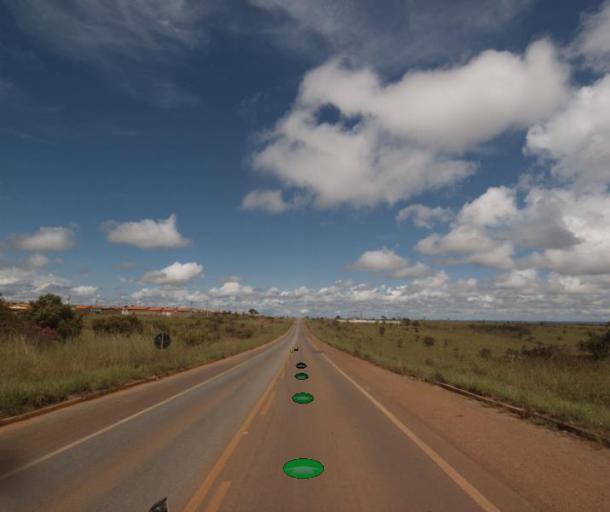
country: BR
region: Federal District
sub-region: Brasilia
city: Brasilia
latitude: -15.7410
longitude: -48.4098
